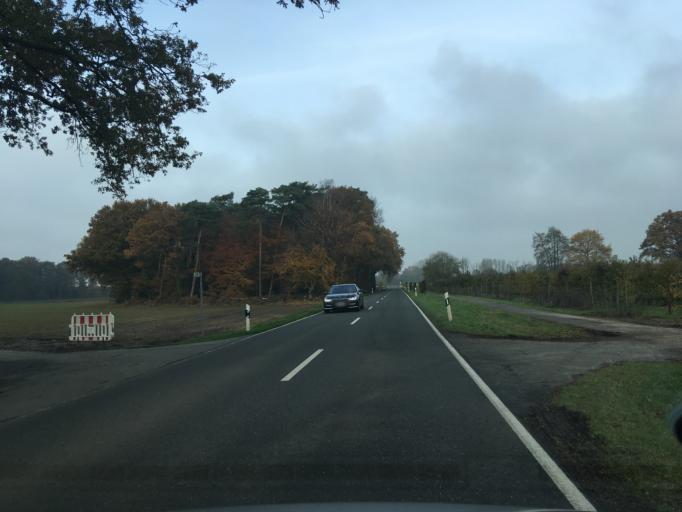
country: DE
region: North Rhine-Westphalia
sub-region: Regierungsbezirk Munster
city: Sudlohn
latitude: 51.9203
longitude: 6.9155
